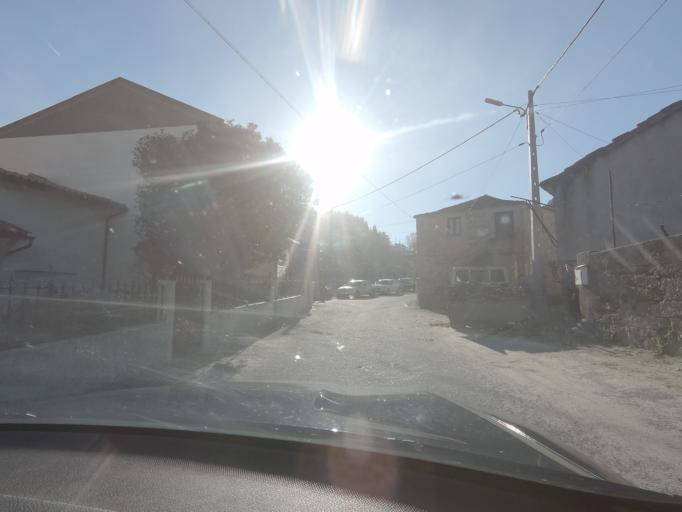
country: PT
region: Viseu
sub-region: Oliveira de Frades
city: Oliveira de Frades
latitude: 40.7344
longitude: -8.1598
